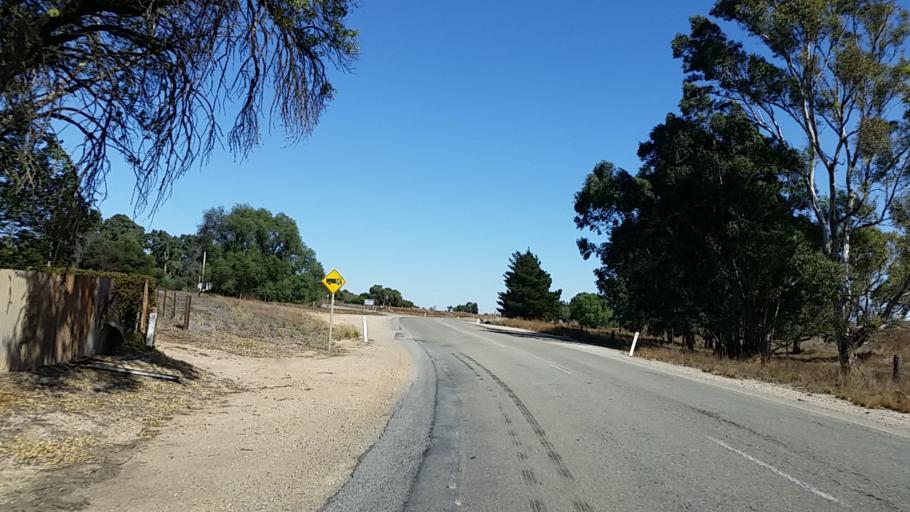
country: AU
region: South Australia
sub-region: Clare and Gilbert Valleys
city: Clare
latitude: -33.6755
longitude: 138.9168
